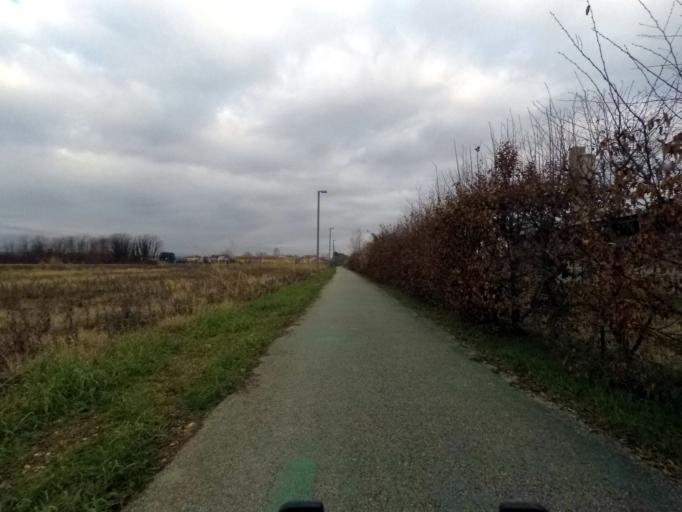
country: IT
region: Friuli Venezia Giulia
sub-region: Provincia di Udine
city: Tavagnacco
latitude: 46.1096
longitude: 13.2133
